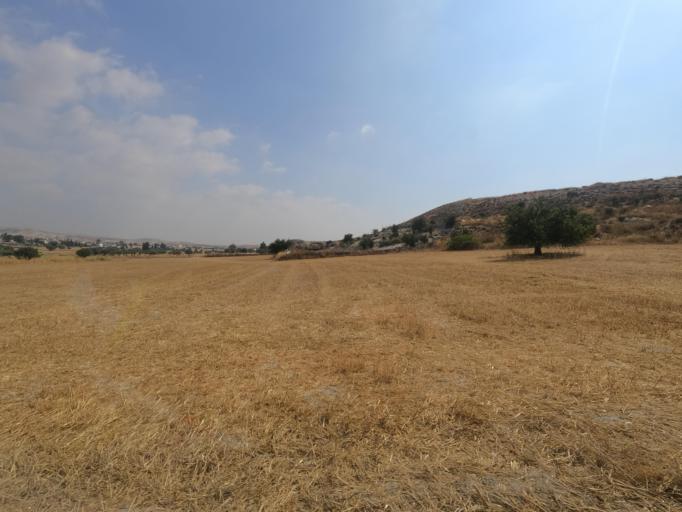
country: CY
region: Larnaka
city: Aradippou
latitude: 34.9178
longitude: 33.5404
